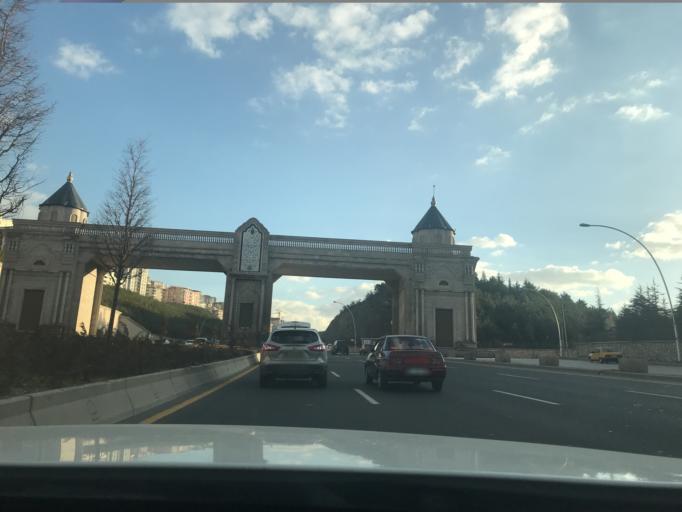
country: TR
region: Ankara
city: Ankara
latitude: 39.8652
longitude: 32.8102
